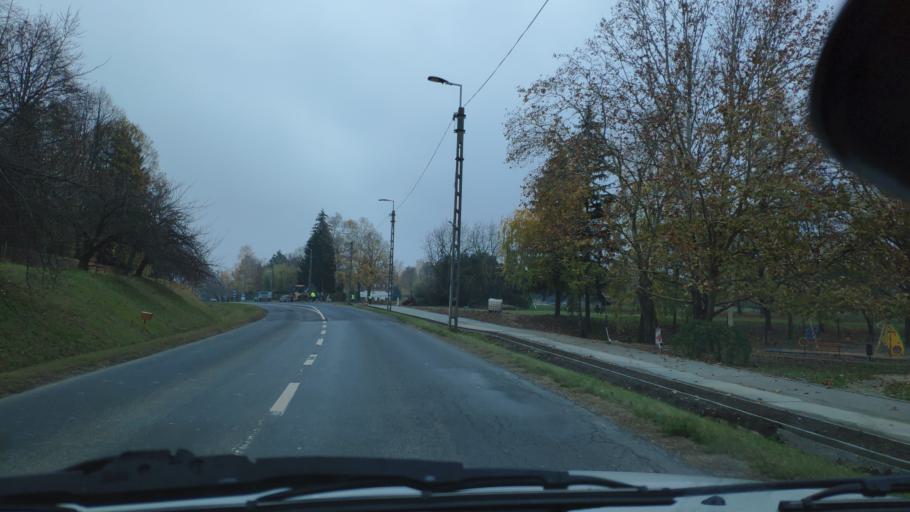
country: HU
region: Zala
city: Zalakomar
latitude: 46.5534
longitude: 17.1214
